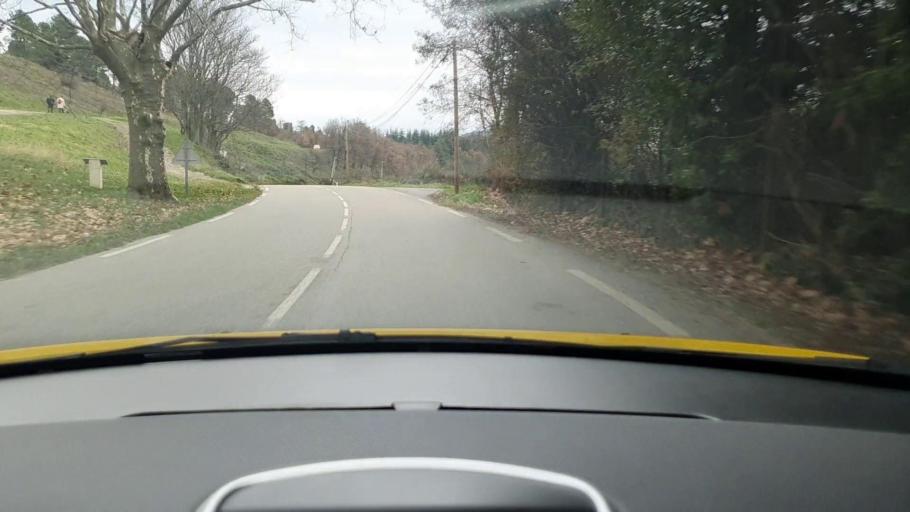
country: FR
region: Languedoc-Roussillon
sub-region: Departement du Gard
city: Branoux-les-Taillades
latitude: 44.2678
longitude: 4.0253
